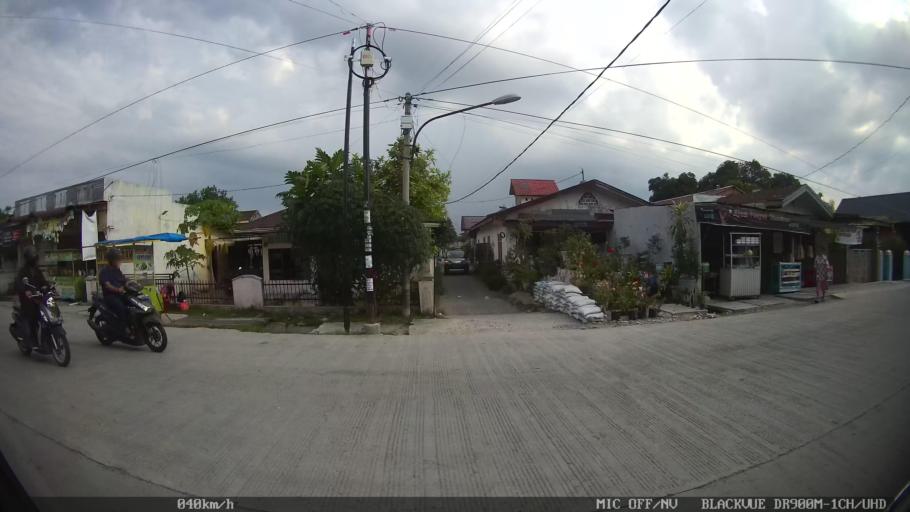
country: ID
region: North Sumatra
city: Sunggal
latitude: 3.5622
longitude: 98.6238
